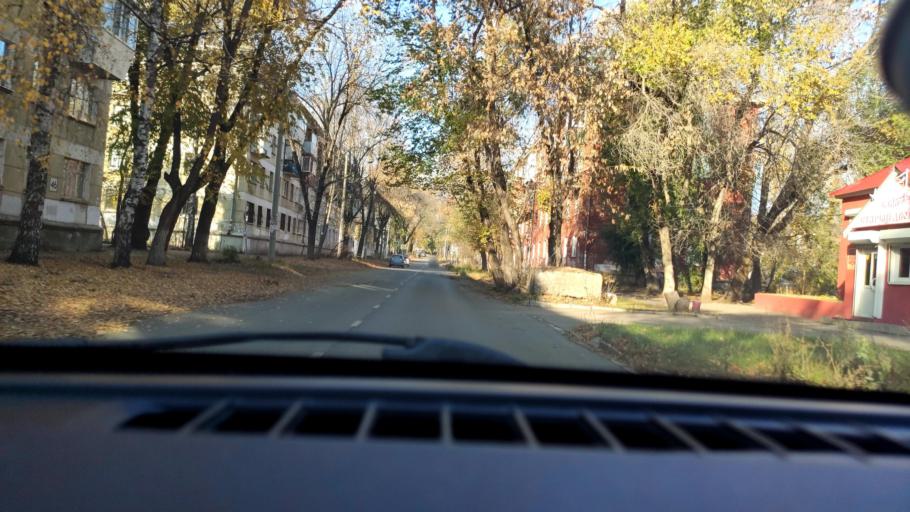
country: RU
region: Samara
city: Samara
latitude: 53.2270
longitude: 50.2595
